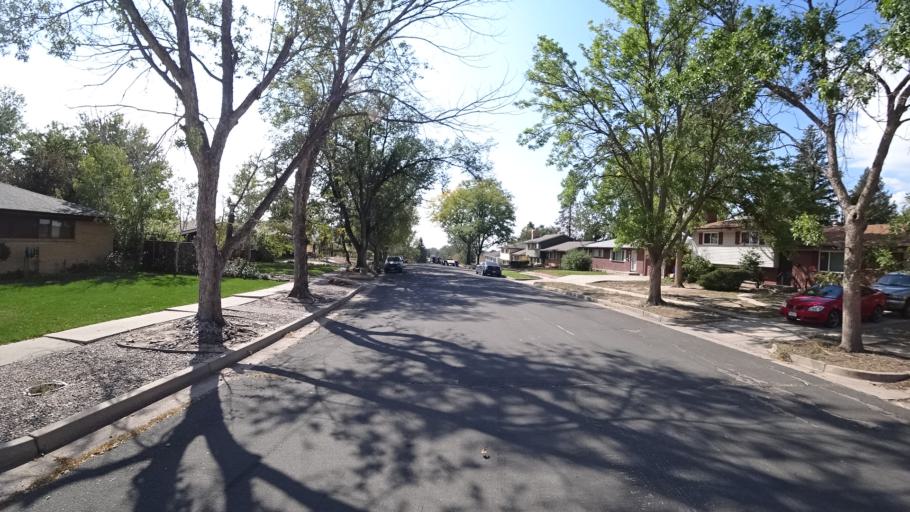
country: US
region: Colorado
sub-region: El Paso County
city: Cimarron Hills
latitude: 38.8614
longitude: -104.7607
